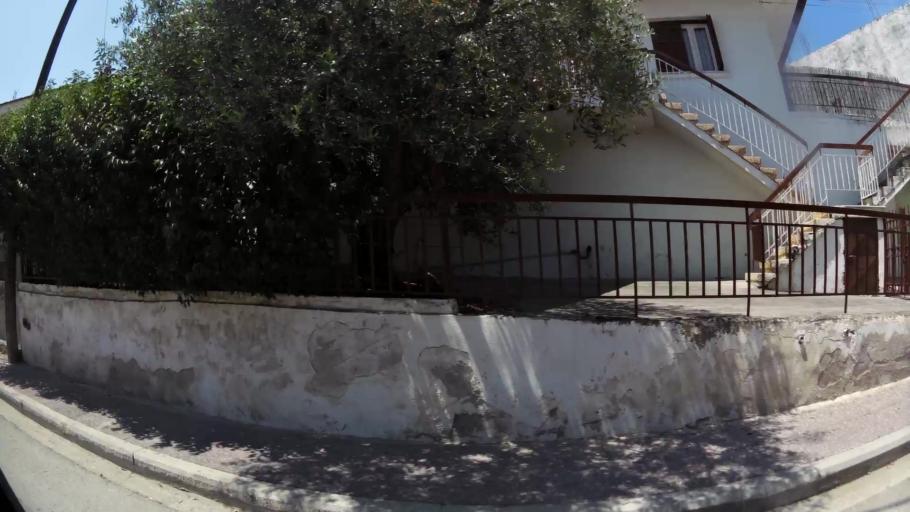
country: GR
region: Central Macedonia
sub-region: Nomos Thessalonikis
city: Epanomi
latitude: 40.4278
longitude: 22.9267
